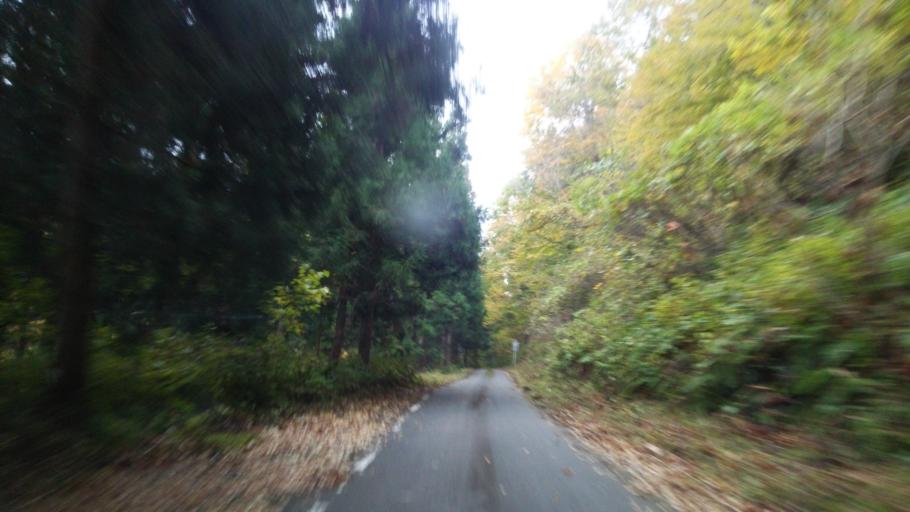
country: JP
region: Fukushima
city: Kitakata
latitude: 37.4073
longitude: 139.7050
